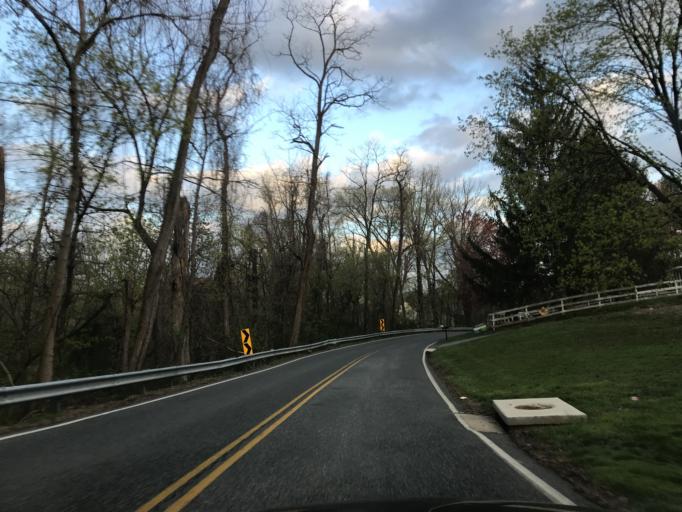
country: US
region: Maryland
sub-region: Harford County
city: South Bel Air
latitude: 39.5318
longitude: -76.3216
